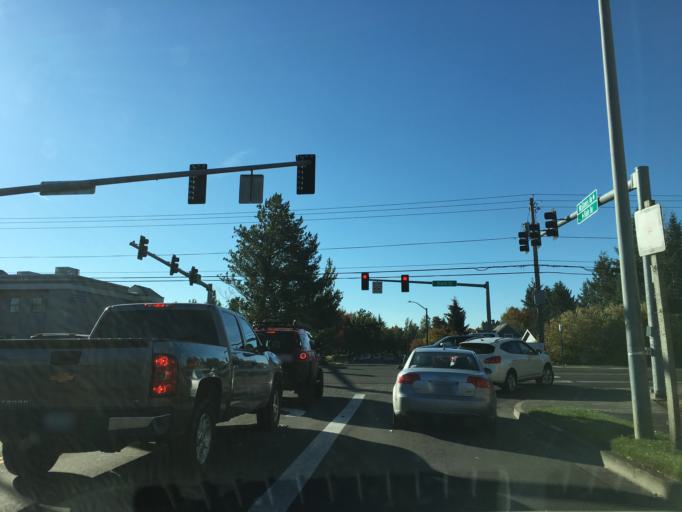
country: US
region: Oregon
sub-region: Multnomah County
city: Wood Village
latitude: 45.5194
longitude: -122.4012
